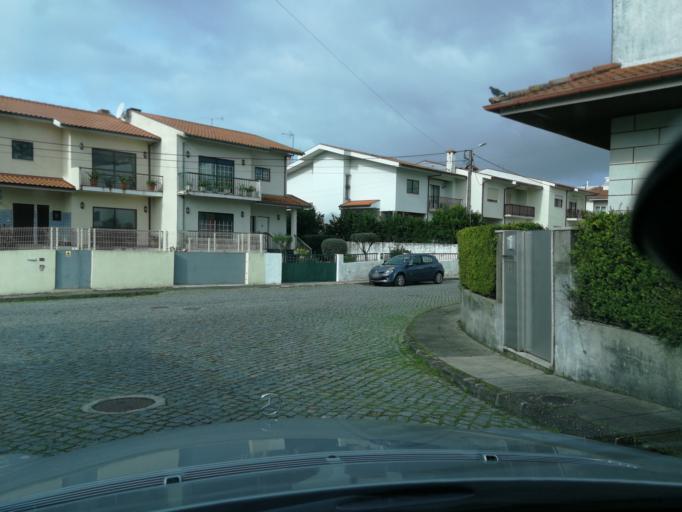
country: PT
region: Braga
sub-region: Braga
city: Braga
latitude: 41.5302
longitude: -8.4077
